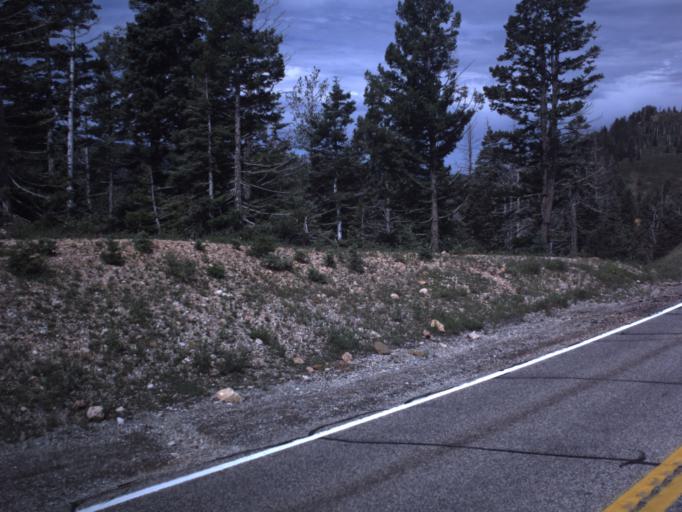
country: US
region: Utah
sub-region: Iron County
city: Cedar City
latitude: 37.5786
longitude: -112.8700
